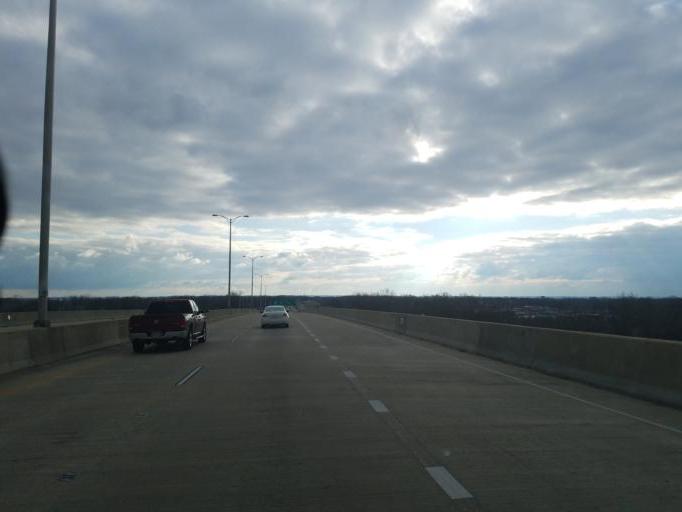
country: US
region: Illinois
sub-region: Madison County
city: Mitchell
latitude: 38.7658
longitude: -90.1349
